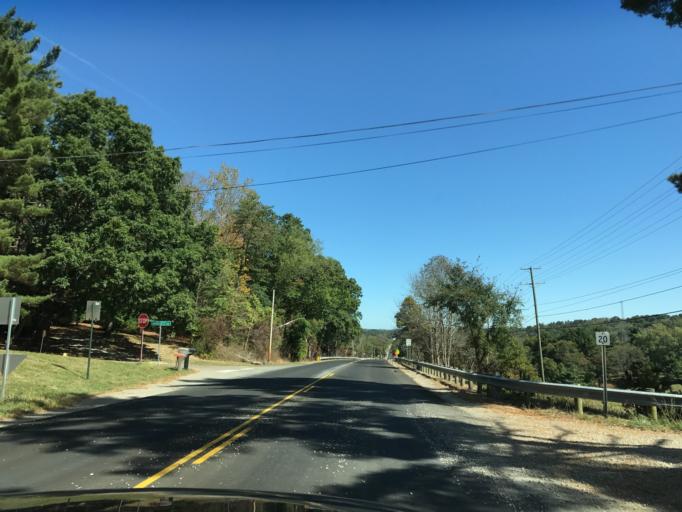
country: US
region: Ohio
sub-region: Muskingum County
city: Pleasant Grove
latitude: 39.9693
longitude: -81.8647
